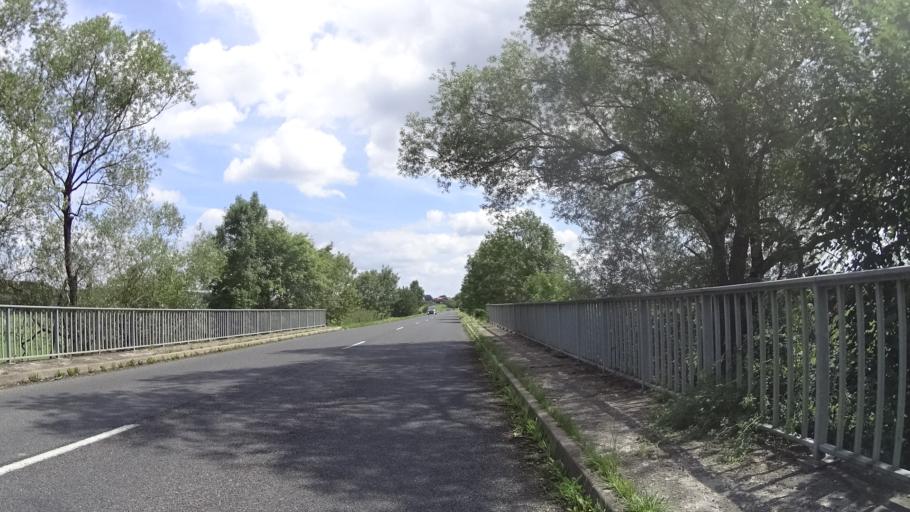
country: FR
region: Lorraine
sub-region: Departement de la Meuse
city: Euville
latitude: 48.7550
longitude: 5.6148
